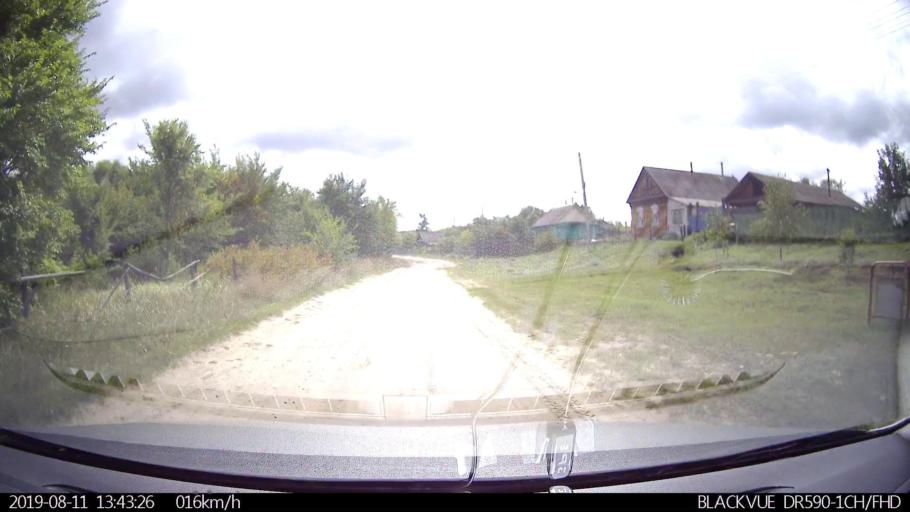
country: RU
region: Ulyanovsk
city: Ignatovka
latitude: 53.8547
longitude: 47.5746
